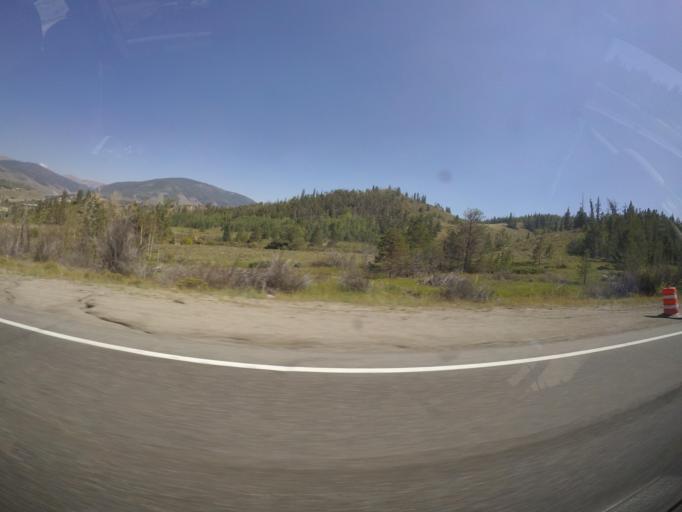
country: US
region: Colorado
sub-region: Summit County
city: Silverthorne
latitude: 39.6225
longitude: -106.0749
